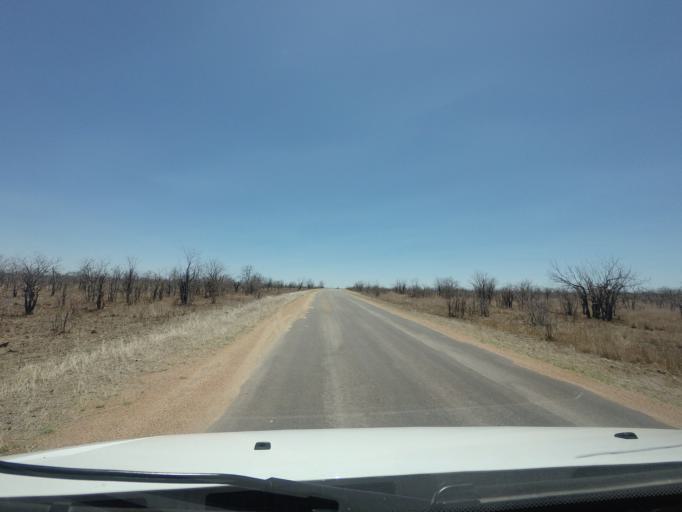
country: ZA
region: Limpopo
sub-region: Mopani District Municipality
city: Phalaborwa
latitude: -23.5825
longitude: 31.4502
